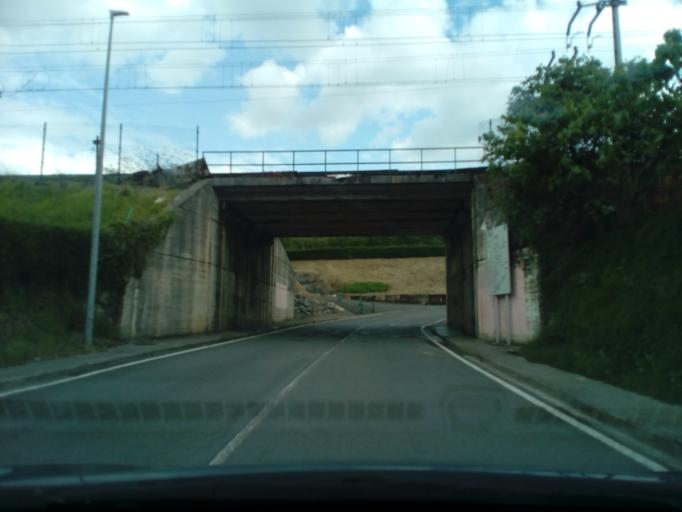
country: ES
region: Basque Country
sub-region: Provincia de Guipuzcoa
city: Andoain
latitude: 43.2124
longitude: -2.0227
